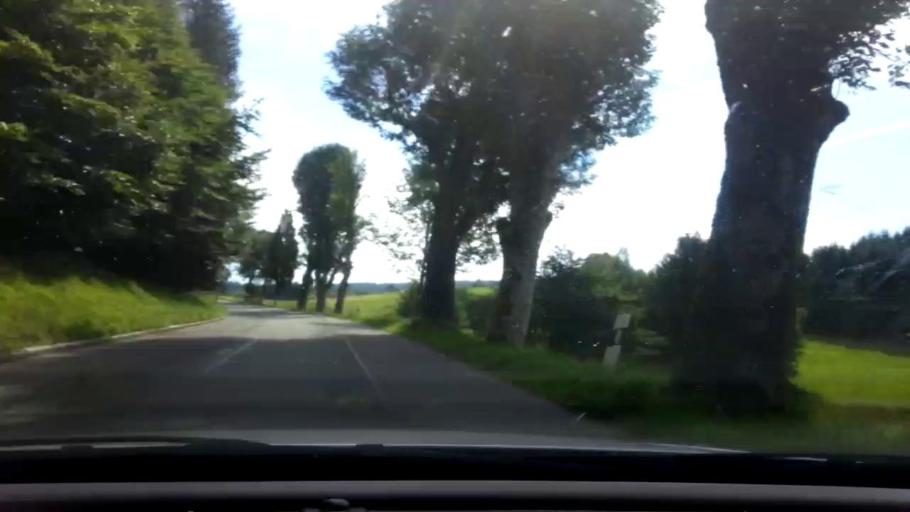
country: DE
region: Bavaria
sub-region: Upper Franconia
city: Bischofsgrun
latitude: 50.0544
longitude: 11.7849
